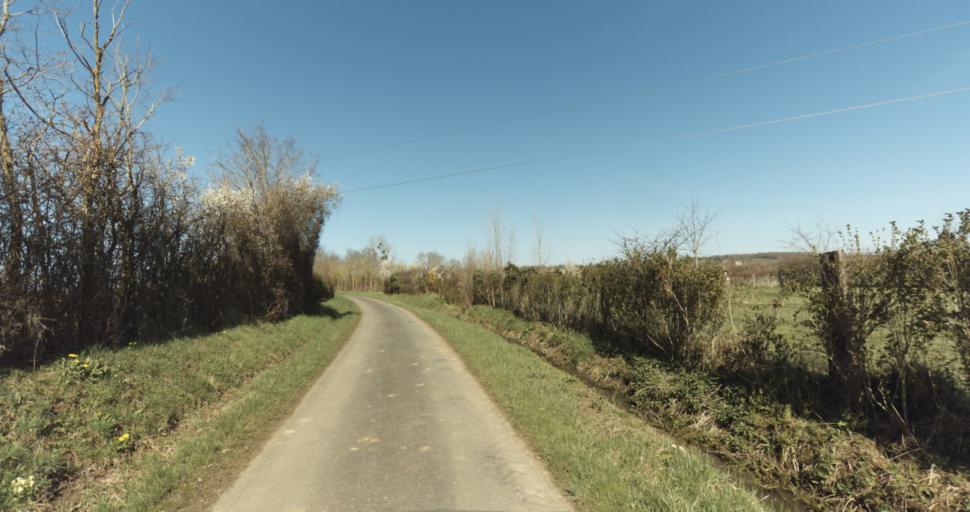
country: FR
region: Lower Normandy
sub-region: Departement du Calvados
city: Saint-Pierre-sur-Dives
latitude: 49.0300
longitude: 0.0198
